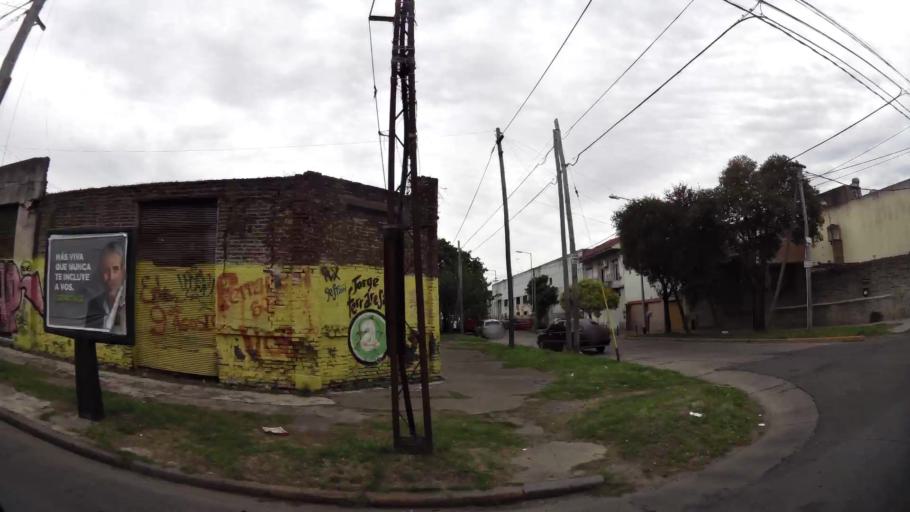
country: AR
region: Buenos Aires
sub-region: Partido de Lanus
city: Lanus
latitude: -34.6746
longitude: -58.3938
